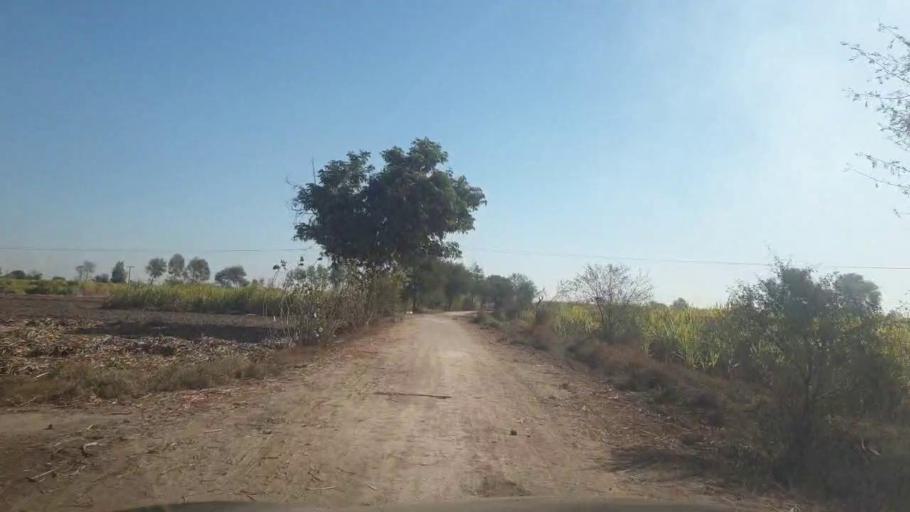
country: PK
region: Sindh
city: Adilpur
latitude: 27.9688
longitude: 69.3346
